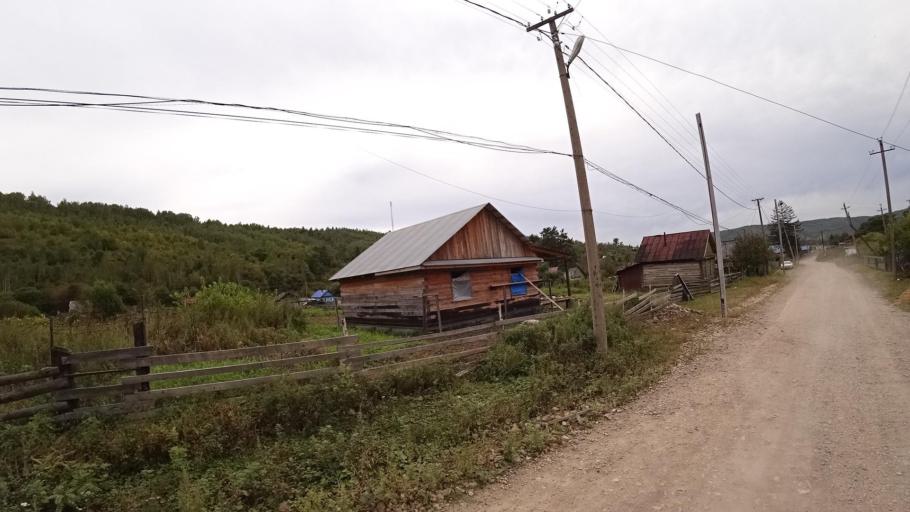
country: RU
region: Jewish Autonomous Oblast
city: Khingansk
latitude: 49.0230
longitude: 131.0691
